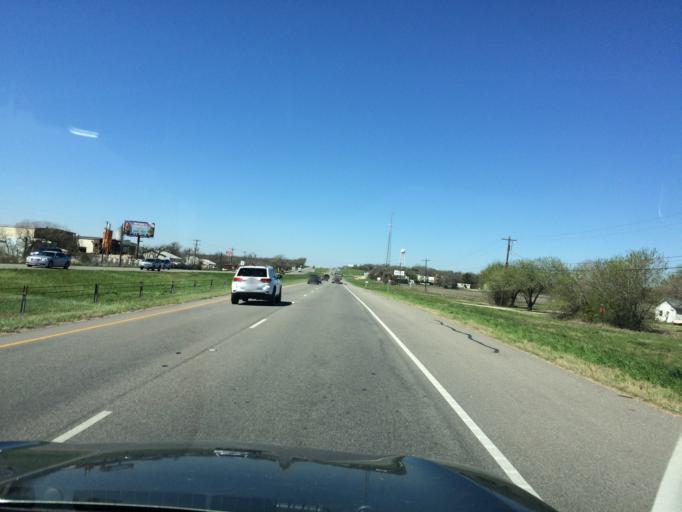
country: US
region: Texas
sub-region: Travis County
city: Garfield
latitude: 30.1854
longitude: -97.5475
